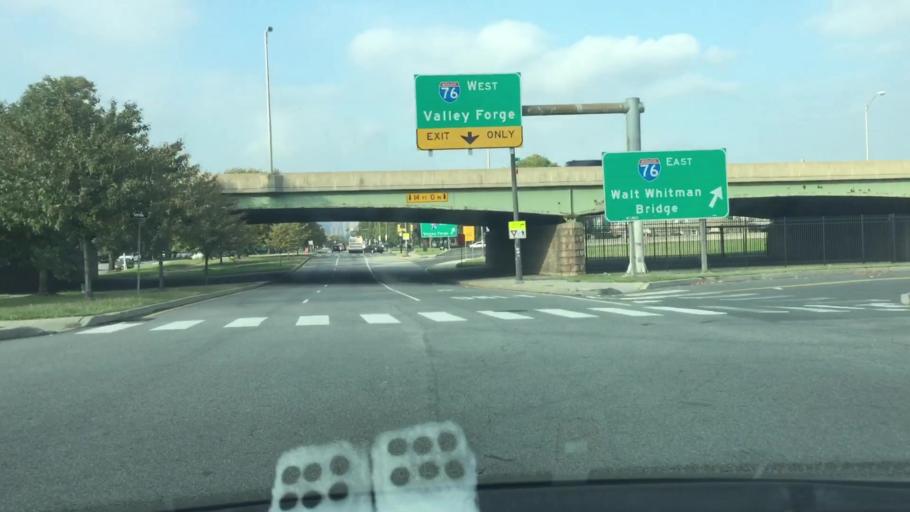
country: US
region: Pennsylvania
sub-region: Philadelphia County
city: Philadelphia
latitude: 39.9118
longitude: -75.1724
